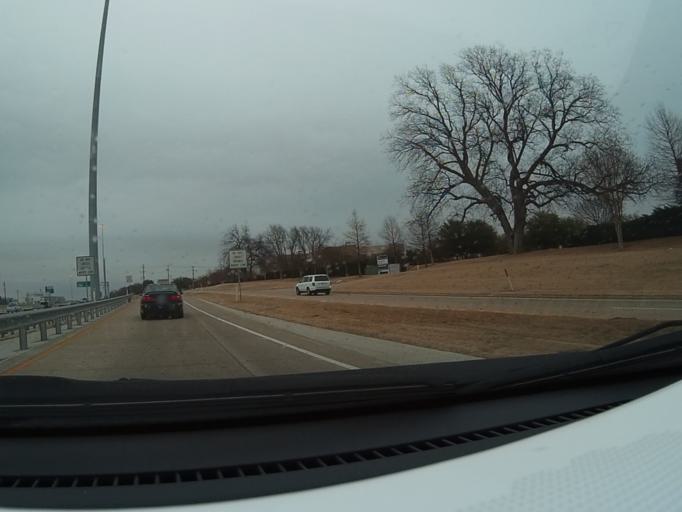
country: US
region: Texas
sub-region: Collin County
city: Allen
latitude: 33.0789
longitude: -96.6847
